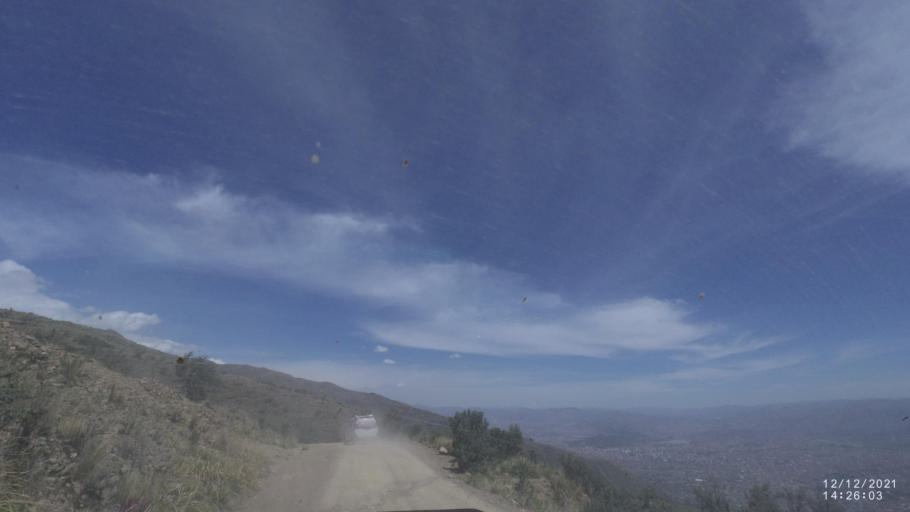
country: BO
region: Cochabamba
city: Cochabamba
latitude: -17.2917
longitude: -66.2184
